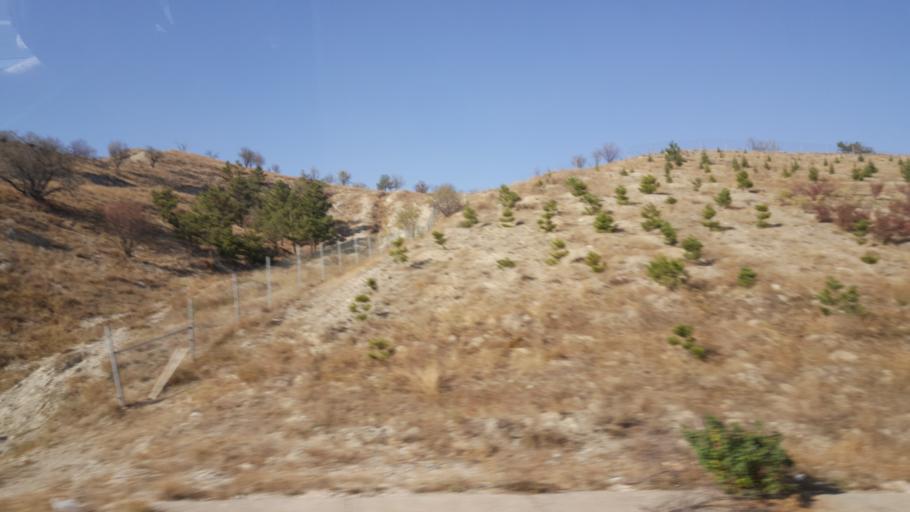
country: TR
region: Ankara
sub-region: Goelbasi
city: Golbasi
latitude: 39.8128
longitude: 32.8061
